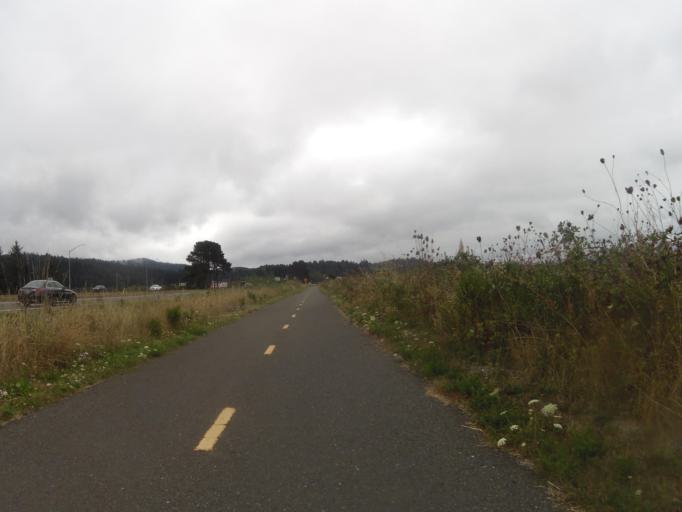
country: US
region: California
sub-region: Humboldt County
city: Bayside
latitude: 40.8348
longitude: -124.0831
